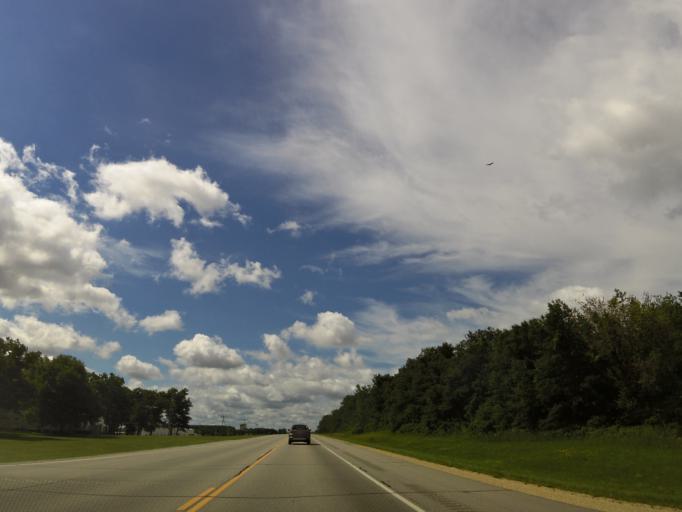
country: US
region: Minnesota
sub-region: Mower County
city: Grand Meadow
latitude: 43.7248
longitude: -92.4793
